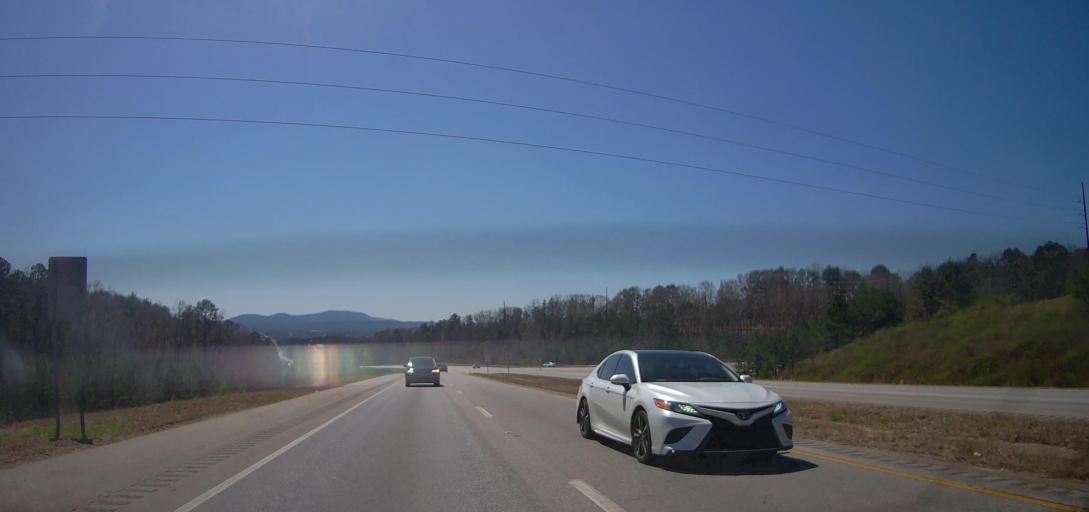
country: US
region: Alabama
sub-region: Calhoun County
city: Anniston
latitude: 33.6516
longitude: -85.7856
